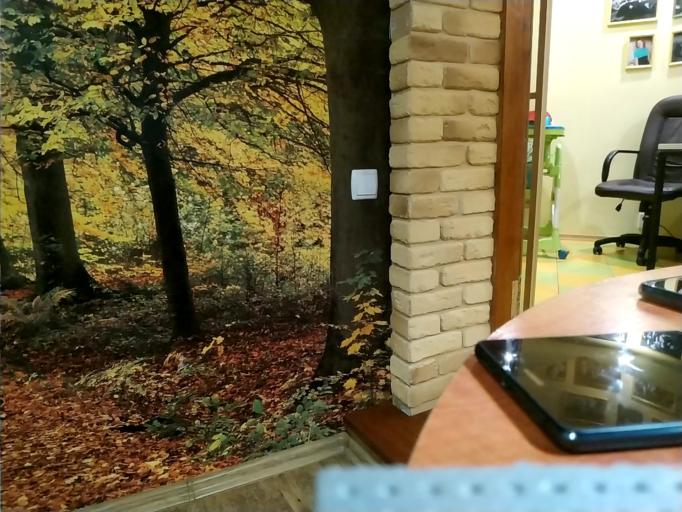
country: RU
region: Tverskaya
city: Zubtsov
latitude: 56.2193
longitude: 34.7110
